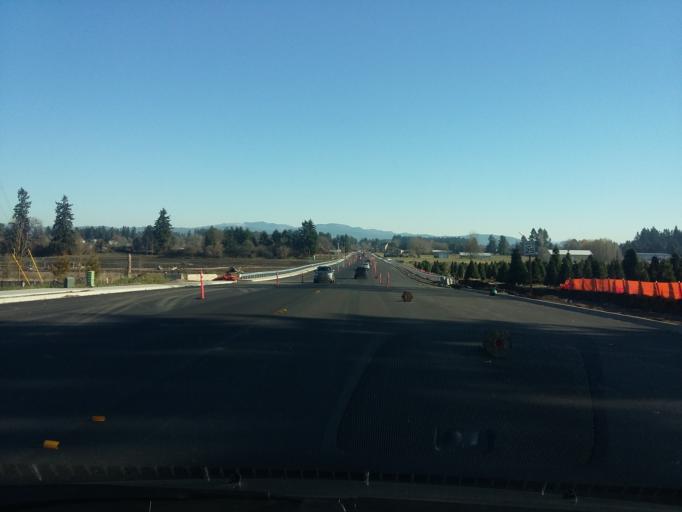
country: US
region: Washington
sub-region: Clark County
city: Barberton
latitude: 45.7078
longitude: -122.5942
